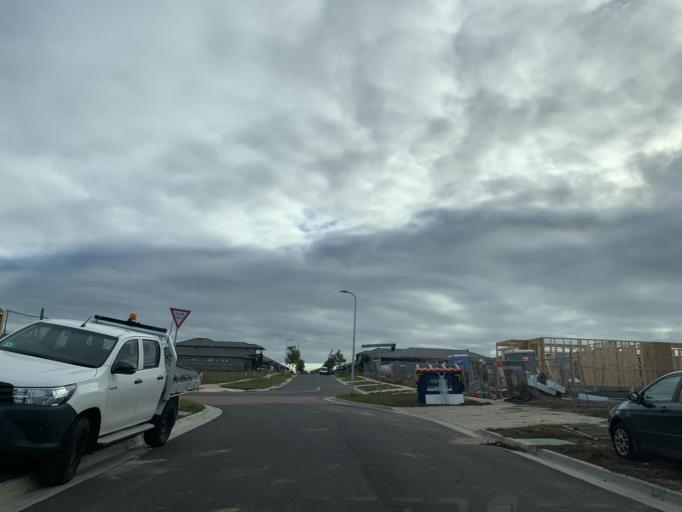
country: AU
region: Victoria
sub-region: Casey
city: Cranbourne East
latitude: -38.1260
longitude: 145.3439
